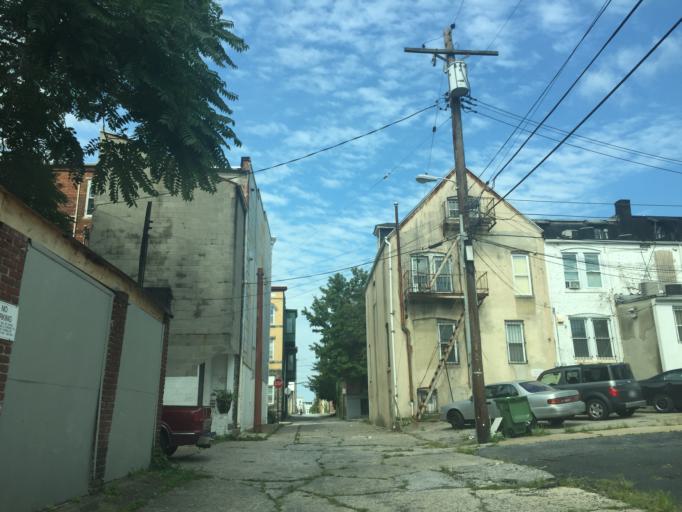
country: US
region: Maryland
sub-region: City of Baltimore
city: Baltimore
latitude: 39.3174
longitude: -76.6136
